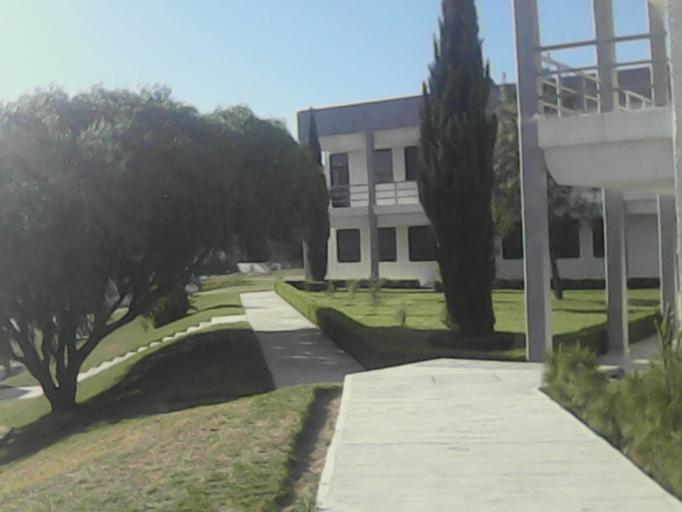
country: MX
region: Hidalgo
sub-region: Mineral de la Reforma
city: Carboneras
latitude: 20.0945
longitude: -98.7084
